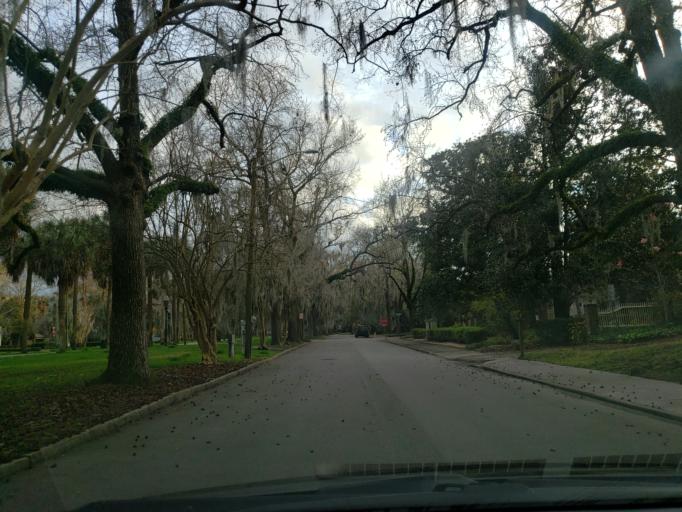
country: US
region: Georgia
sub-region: Chatham County
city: Savannah
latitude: 32.0489
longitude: -81.0920
